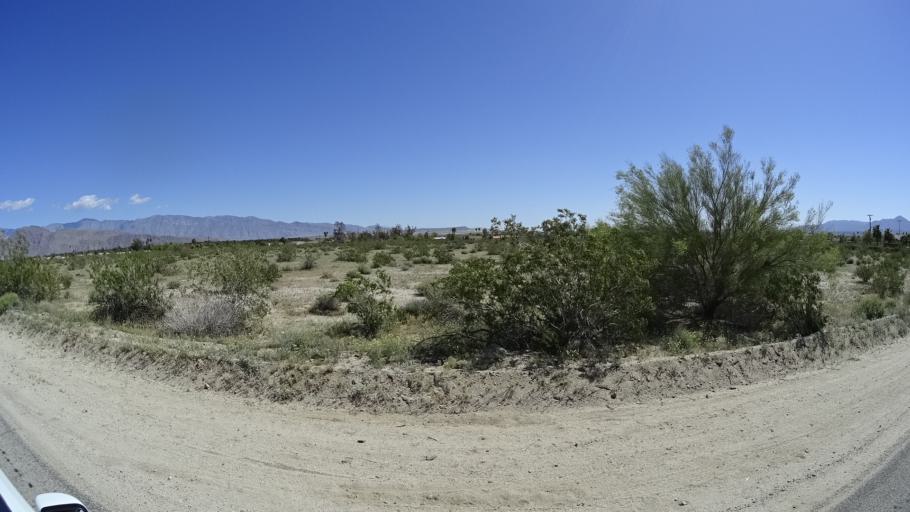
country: US
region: California
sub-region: San Diego County
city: Borrego Springs
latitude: 33.2493
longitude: -116.3765
